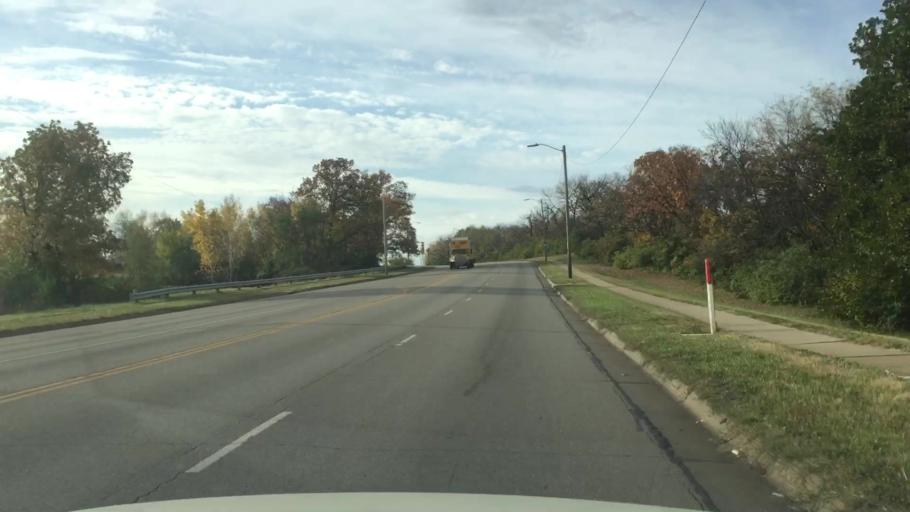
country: US
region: Kansas
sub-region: Shawnee County
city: Topeka
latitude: 39.0367
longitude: -95.6693
